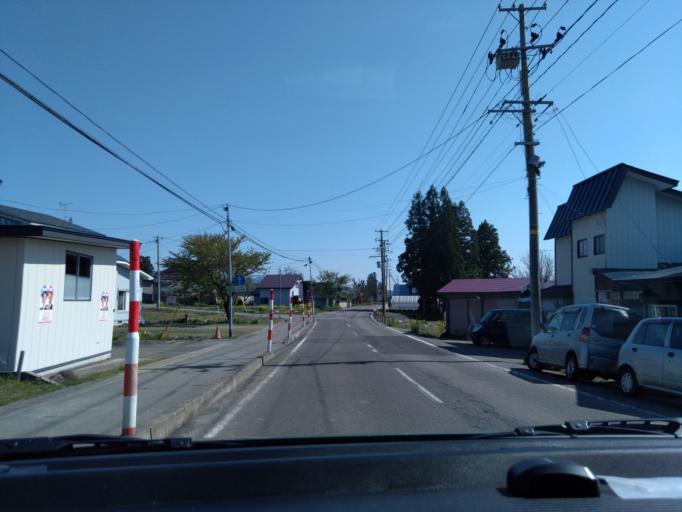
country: JP
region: Akita
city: Kakunodatemachi
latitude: 39.4946
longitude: 140.5941
